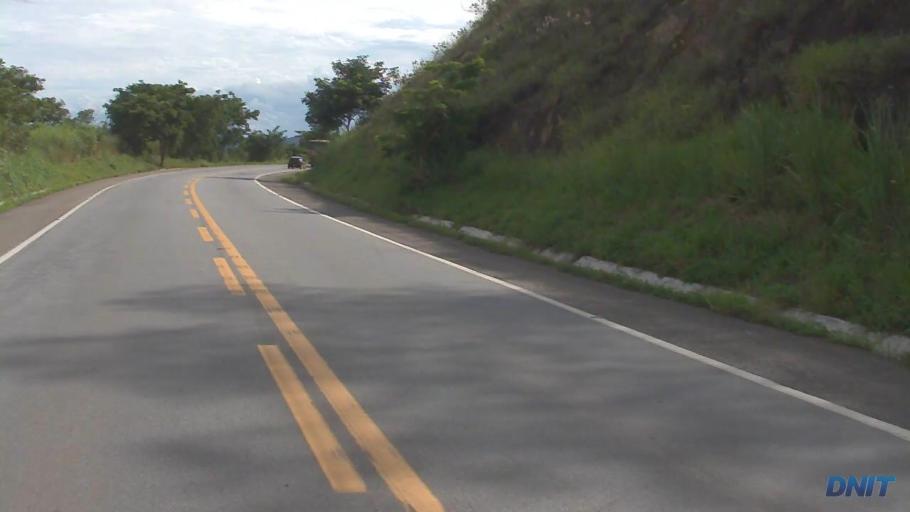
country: BR
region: Minas Gerais
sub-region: Belo Oriente
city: Belo Oriente
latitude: -19.1803
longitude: -42.2599
